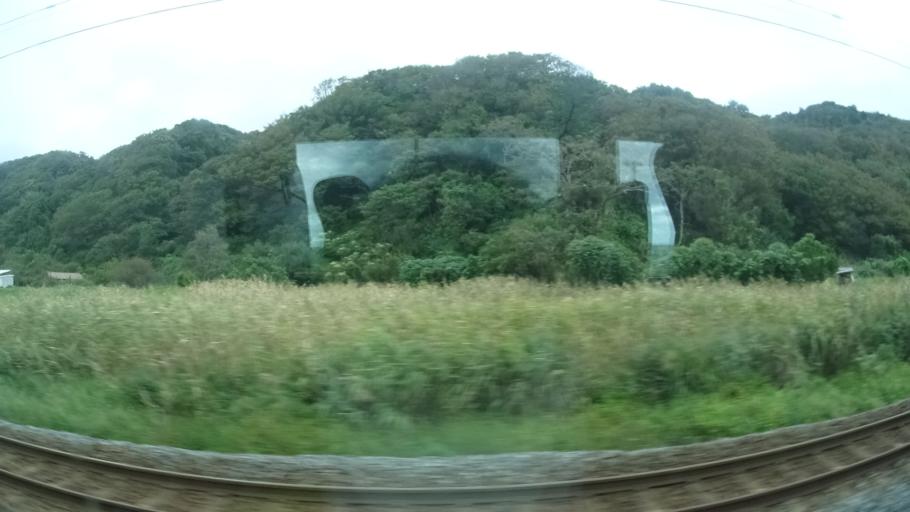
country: JP
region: Niigata
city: Murakami
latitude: 38.3189
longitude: 139.4501
